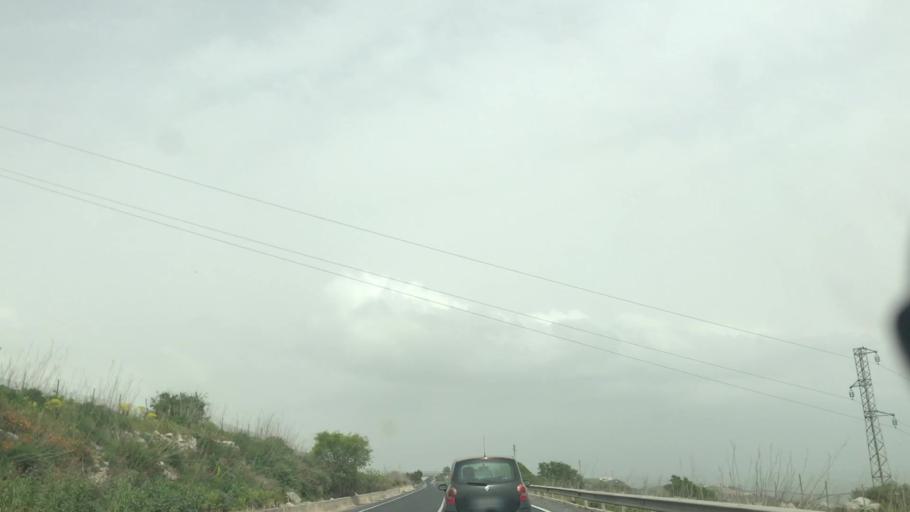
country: IT
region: Sicily
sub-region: Ragusa
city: Ragusa
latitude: 36.8728
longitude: 14.6893
